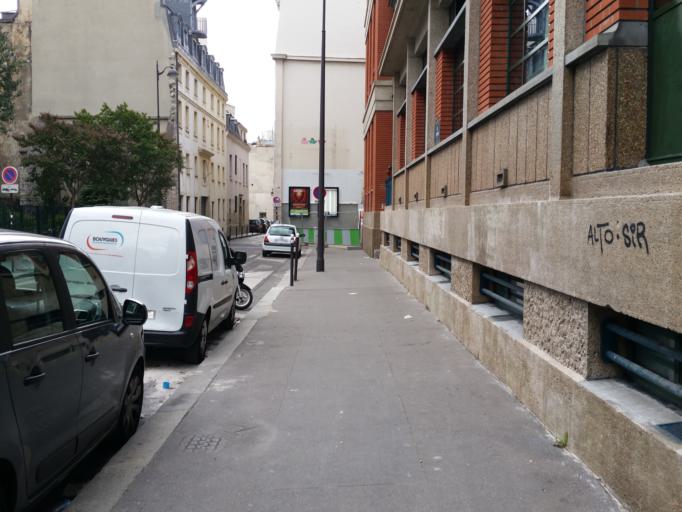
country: FR
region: Ile-de-France
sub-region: Paris
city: Paris
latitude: 48.8435
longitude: 2.3463
